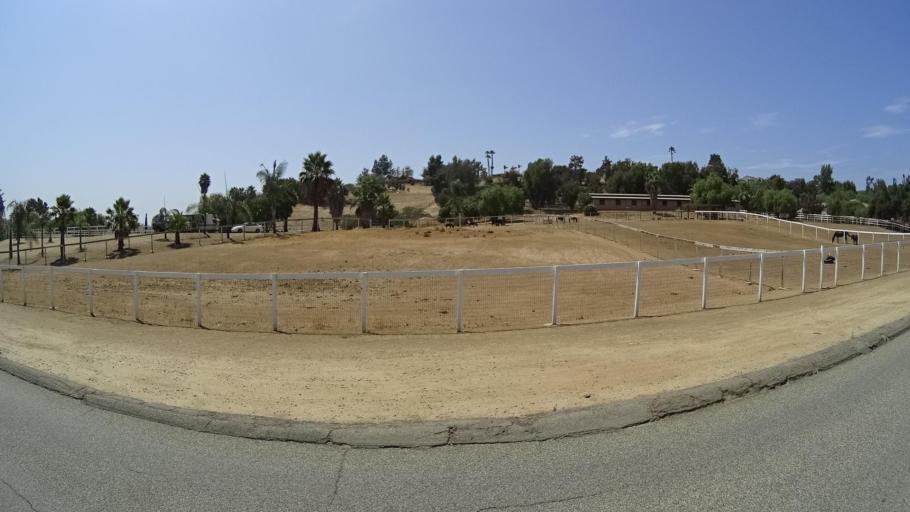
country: US
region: California
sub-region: San Diego County
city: Bonsall
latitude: 33.3117
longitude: -117.2050
